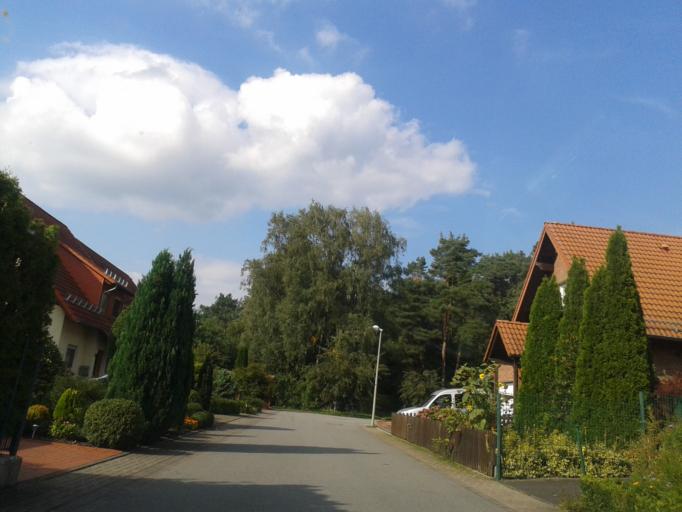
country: DE
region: North Rhine-Westphalia
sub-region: Regierungsbezirk Detmold
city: Schlangen
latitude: 51.8035
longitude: 8.8306
